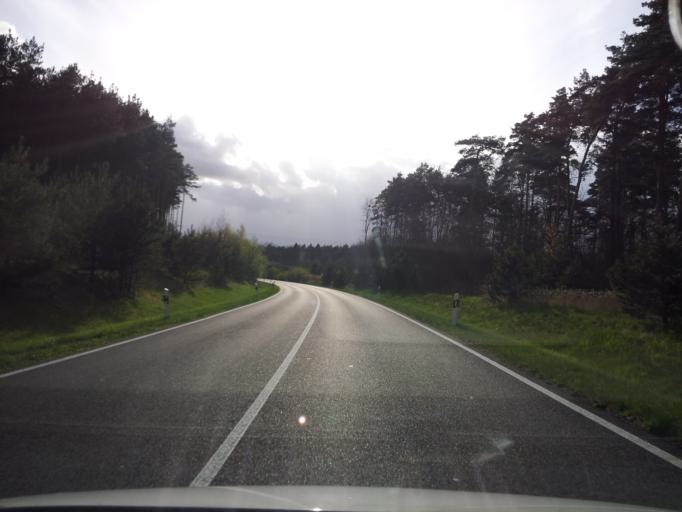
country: DE
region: Brandenburg
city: Schenkendobern
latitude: 51.8985
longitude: 14.6047
